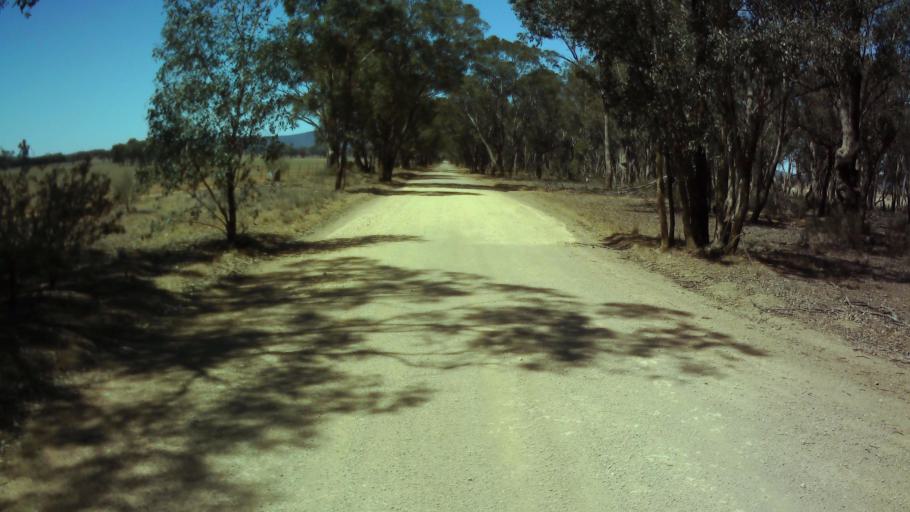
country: AU
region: New South Wales
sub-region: Weddin
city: Grenfell
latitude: -33.8946
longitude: 148.0851
